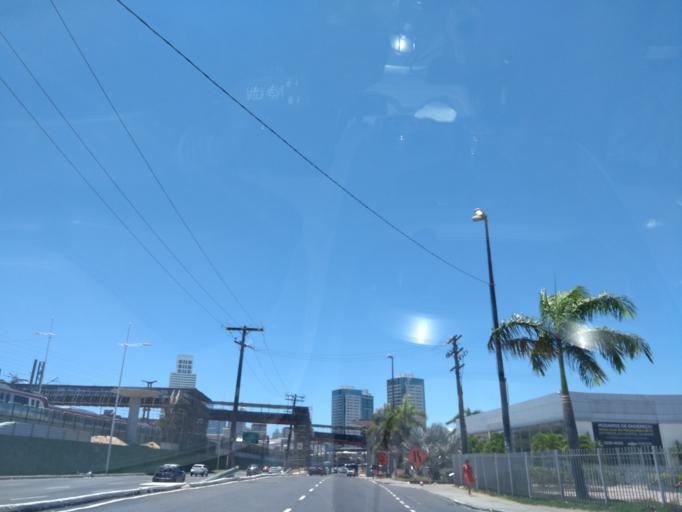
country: BR
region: Bahia
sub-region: Salvador
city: Salvador
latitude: -12.9744
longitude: -38.4519
